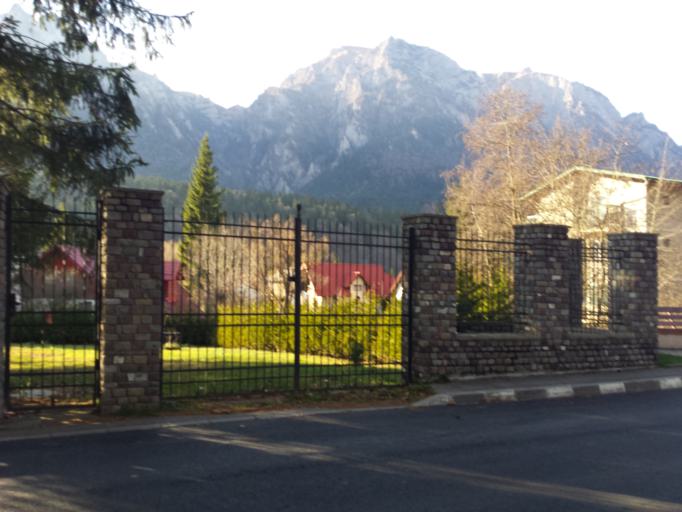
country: RO
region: Prahova
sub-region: Oras Busteni
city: Busteni
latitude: 45.4040
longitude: 25.5402
